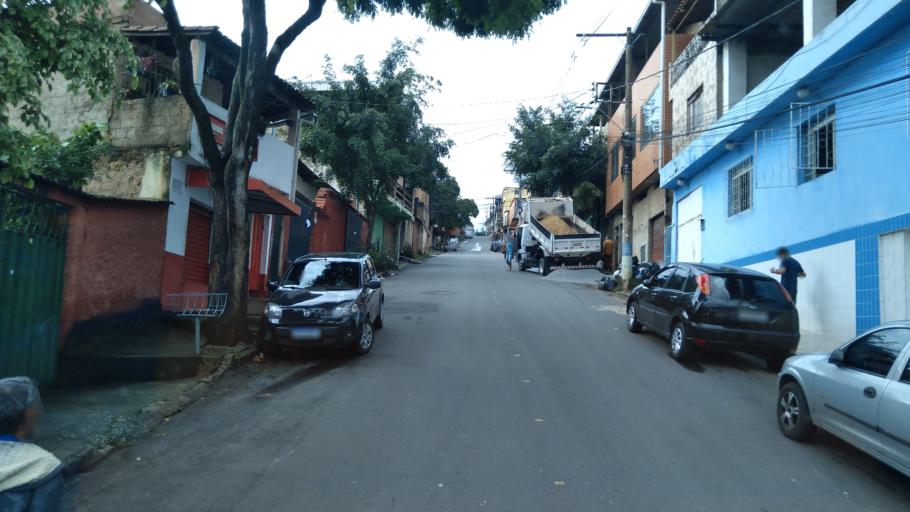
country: BR
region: Minas Gerais
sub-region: Belo Horizonte
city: Belo Horizonte
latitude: -19.9052
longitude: -43.8925
